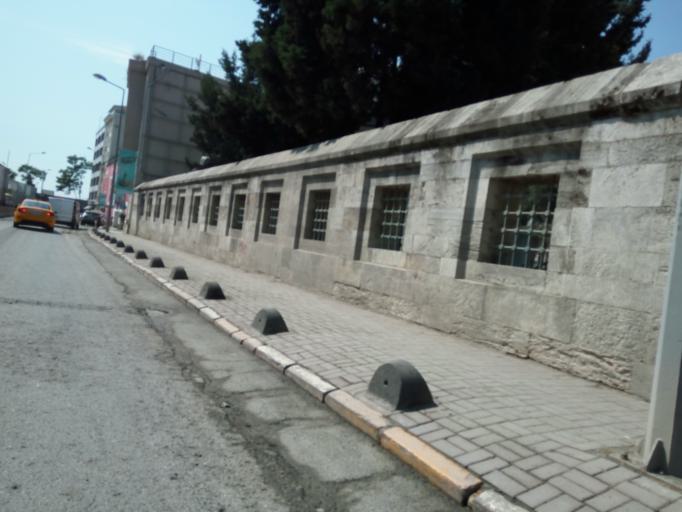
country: TR
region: Istanbul
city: Eminoenue
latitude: 41.0265
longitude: 28.9813
